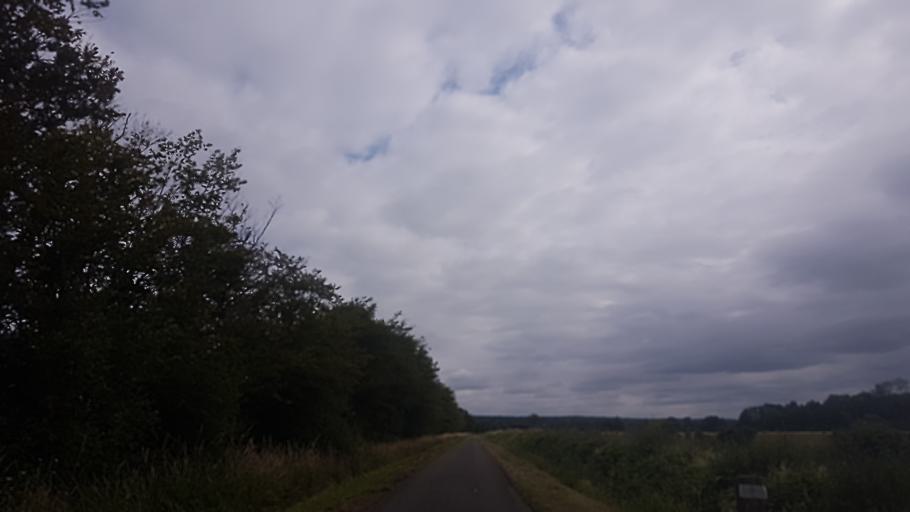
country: BE
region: Wallonia
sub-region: Province de Namur
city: Couvin
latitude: 50.0985
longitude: 4.5411
